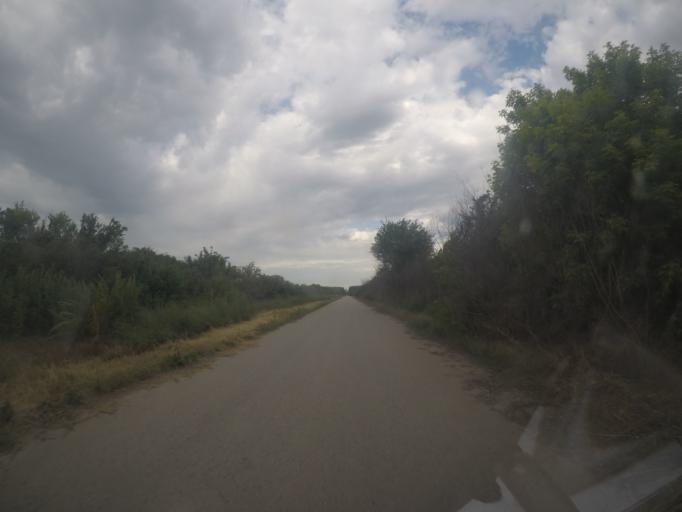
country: RS
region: Central Serbia
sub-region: Belgrade
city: Zemun
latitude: 44.8940
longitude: 20.3885
